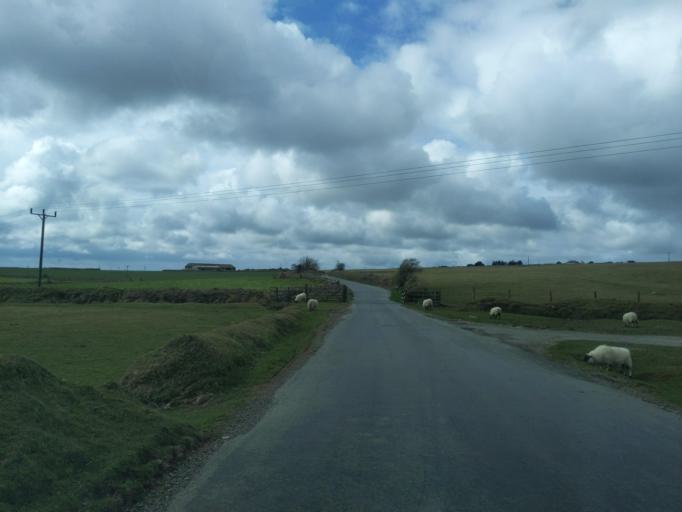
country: GB
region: England
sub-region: Cornwall
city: Camelford
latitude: 50.6403
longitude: -4.6330
